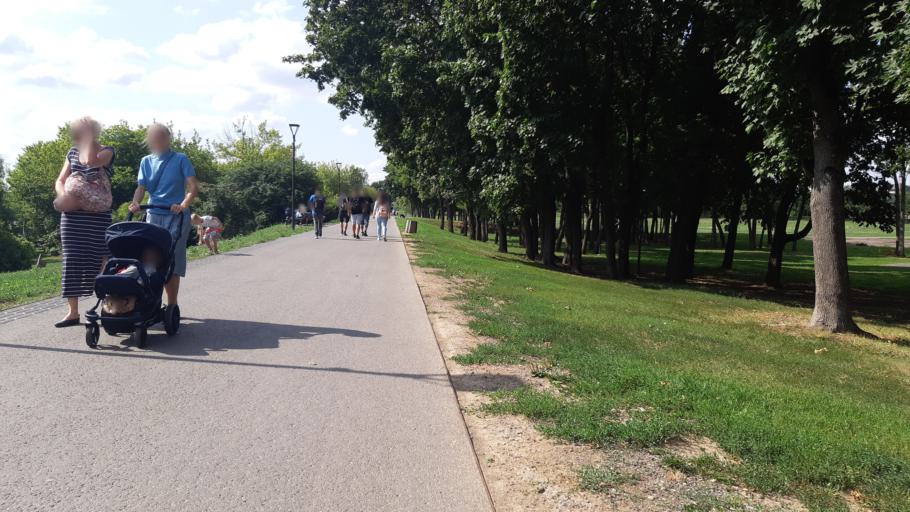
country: LT
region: Kauno apskritis
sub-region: Kaunas
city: Kaunas
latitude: 54.8961
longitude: 23.8812
